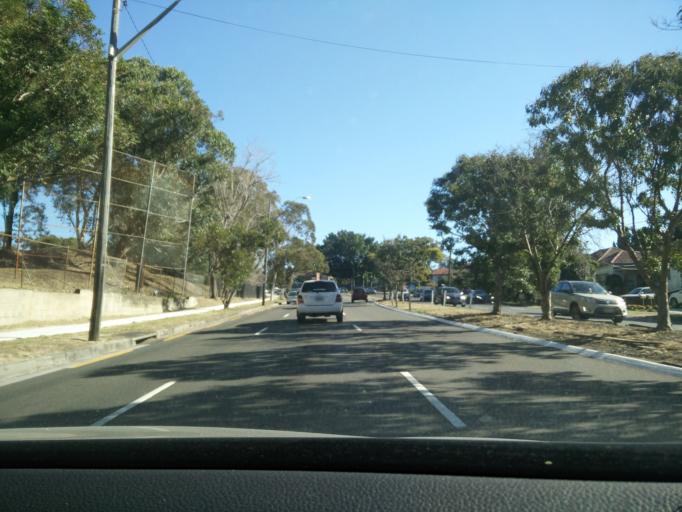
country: AU
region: New South Wales
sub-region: Ryde
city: North Ryde
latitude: -33.7966
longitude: 151.1161
